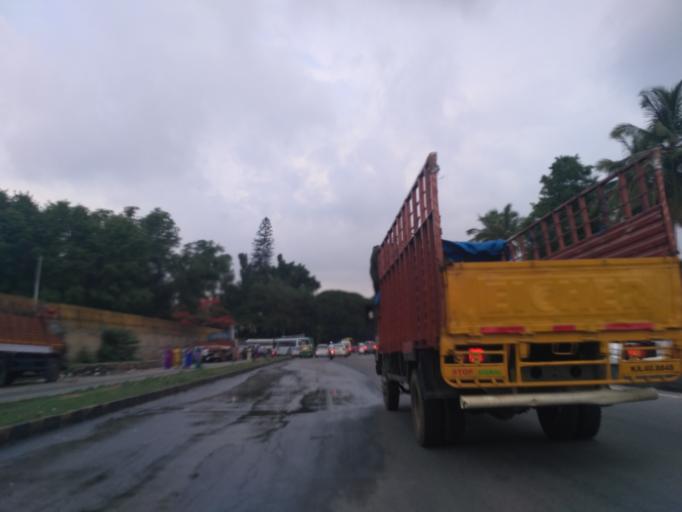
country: IN
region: Karnataka
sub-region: Bangalore Urban
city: Bangalore
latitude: 13.0241
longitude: 77.5336
